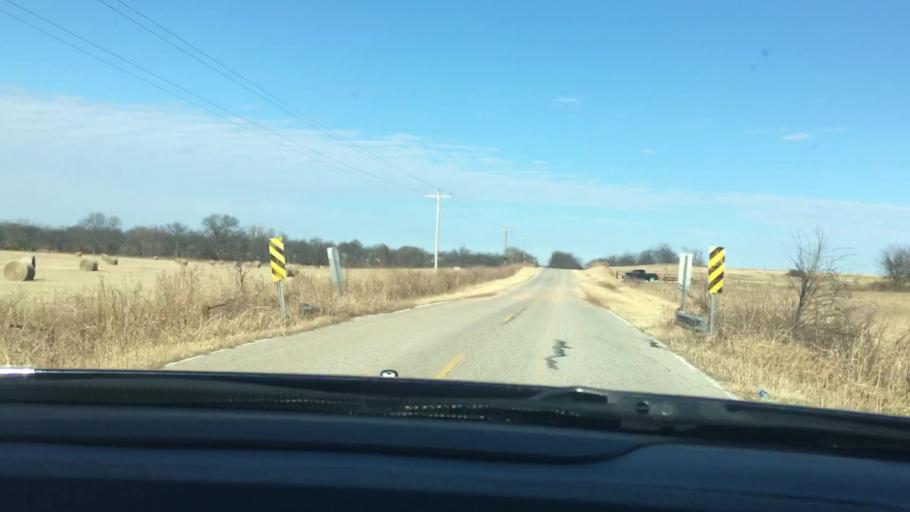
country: US
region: Oklahoma
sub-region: Garvin County
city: Wynnewood
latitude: 34.7173
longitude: -97.1254
